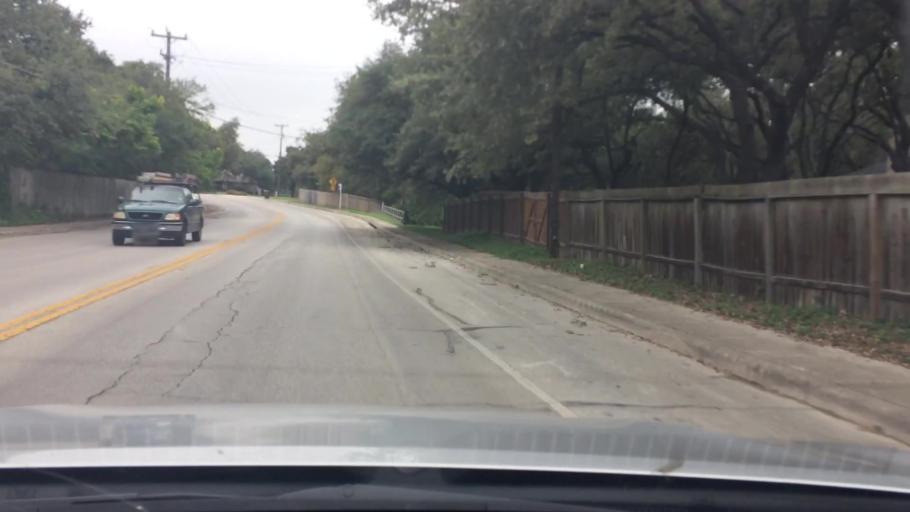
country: US
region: Texas
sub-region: Bexar County
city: Hollywood Park
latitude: 29.5829
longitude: -98.4543
